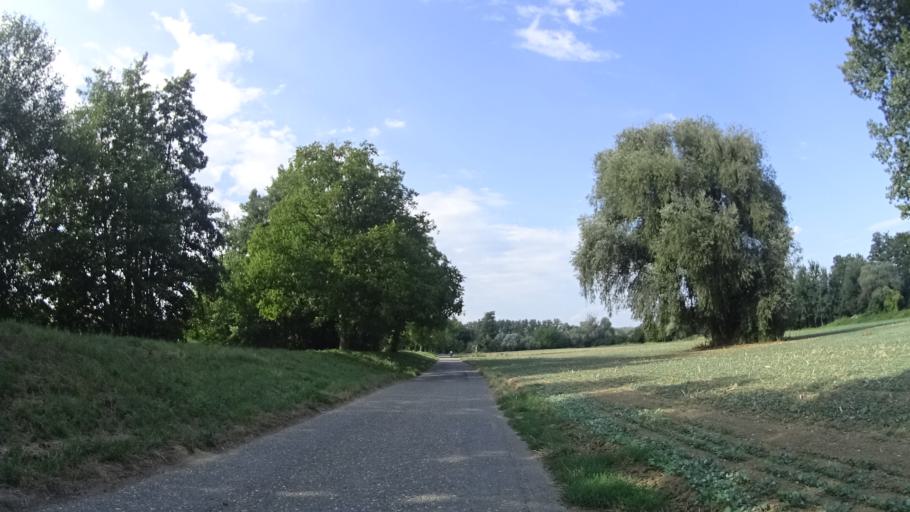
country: CZ
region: Zlin
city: Spytihnev
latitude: 49.1422
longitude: 17.5055
